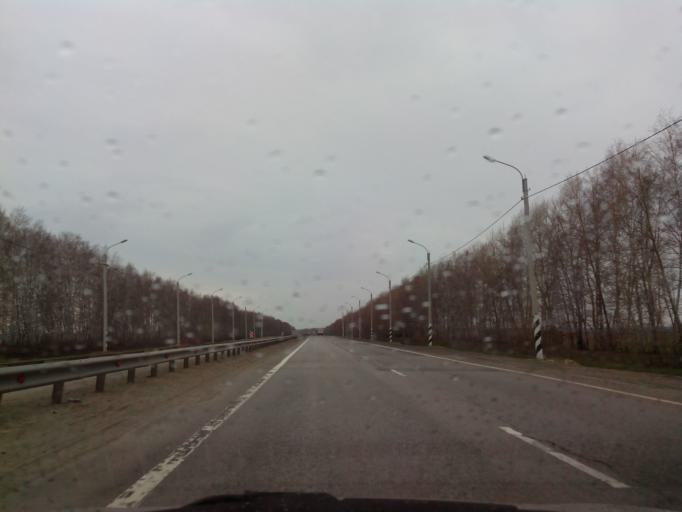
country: RU
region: Tambov
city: Selezni
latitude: 52.7613
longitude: 41.1287
